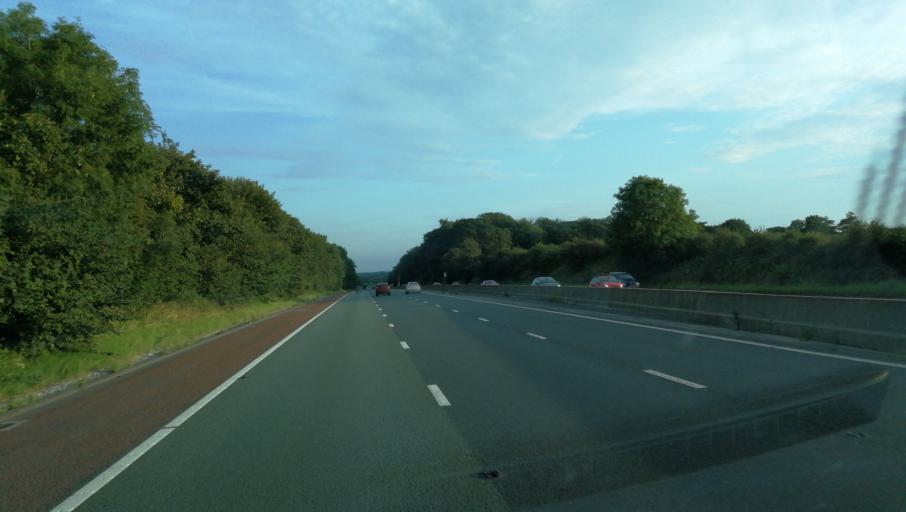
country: GB
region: England
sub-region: Lancashire
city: Galgate
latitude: 54.0169
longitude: -2.7823
